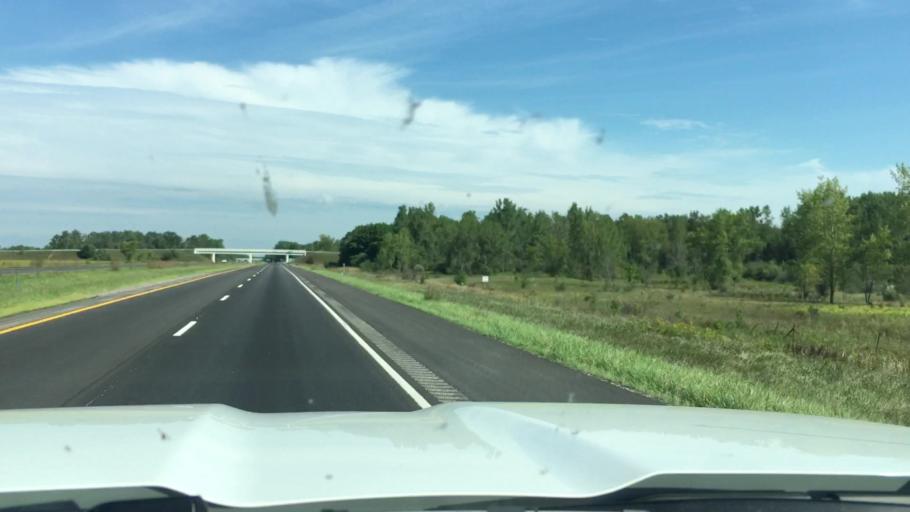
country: US
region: Michigan
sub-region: Saginaw County
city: Freeland
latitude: 43.5641
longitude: -84.1388
